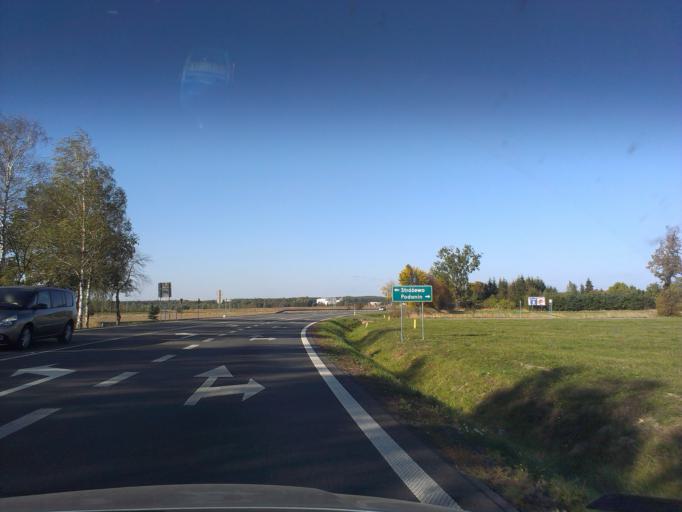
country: PL
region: Greater Poland Voivodeship
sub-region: Powiat chodzieski
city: Chodziez
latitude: 52.9509
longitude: 16.9409
